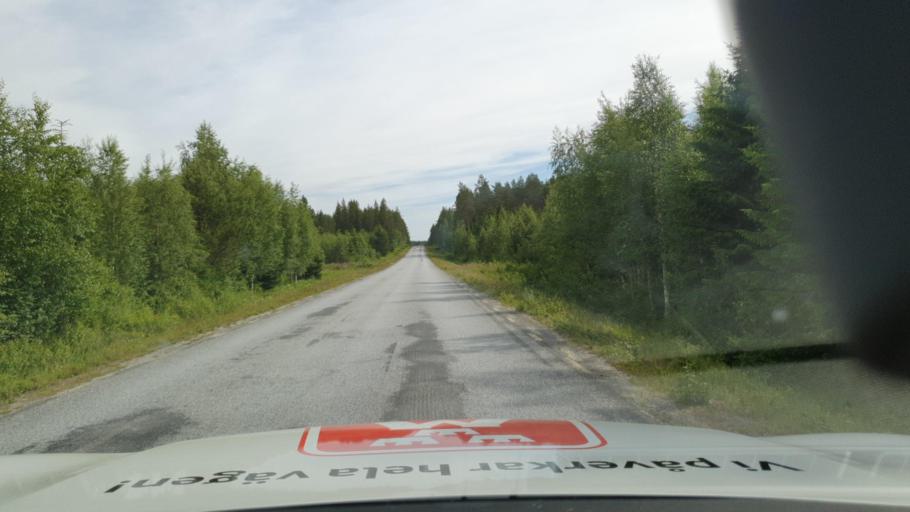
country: SE
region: Vaesterbotten
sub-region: Umea Kommun
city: Saevar
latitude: 63.8901
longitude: 20.7411
